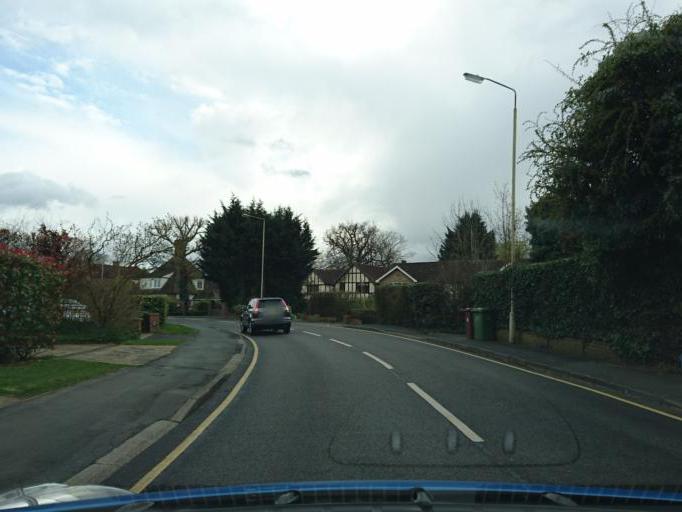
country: GB
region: England
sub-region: Hertfordshire
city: Borehamwood
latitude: 51.6510
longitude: -0.2823
